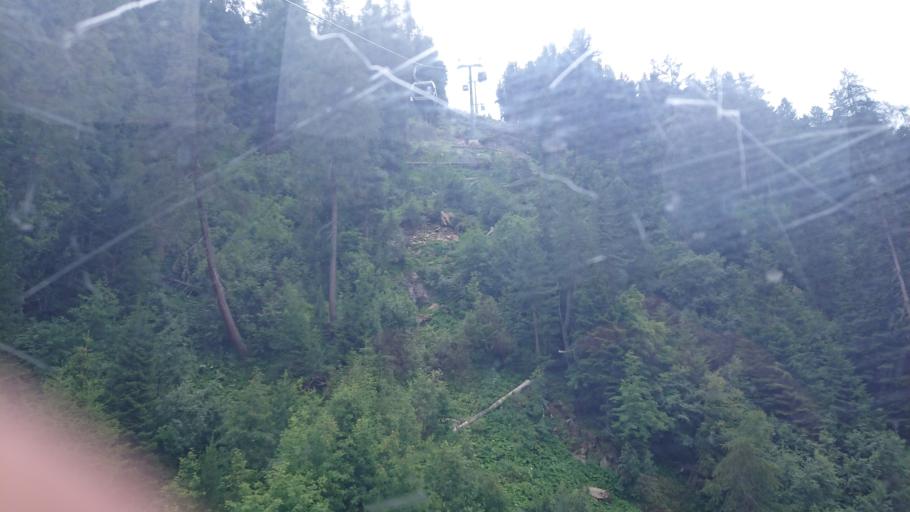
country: AT
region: Tyrol
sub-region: Politischer Bezirk Imst
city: Oetz
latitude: 47.2208
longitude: 10.9323
